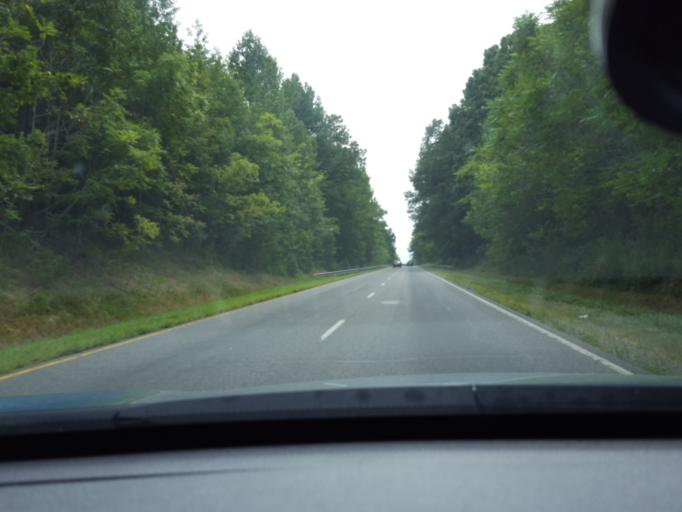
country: US
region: Virginia
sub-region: Caroline County
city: Bowling Green
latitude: 38.1308
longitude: -77.2392
